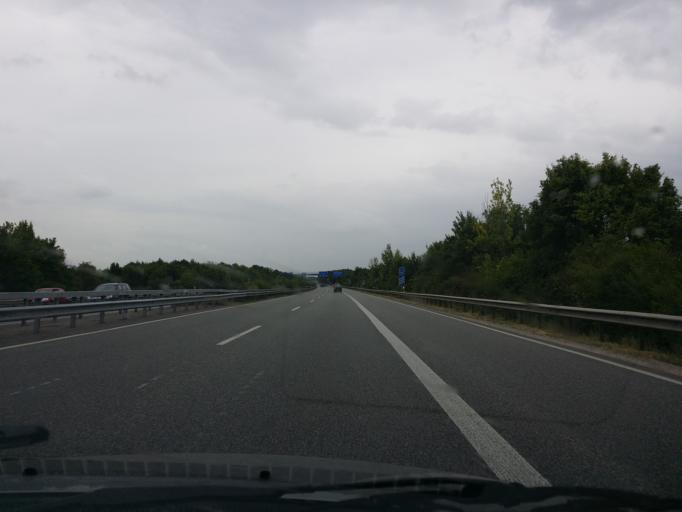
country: DE
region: Rheinland-Pfalz
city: Nieder-Olm
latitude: 49.9174
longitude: 8.1940
